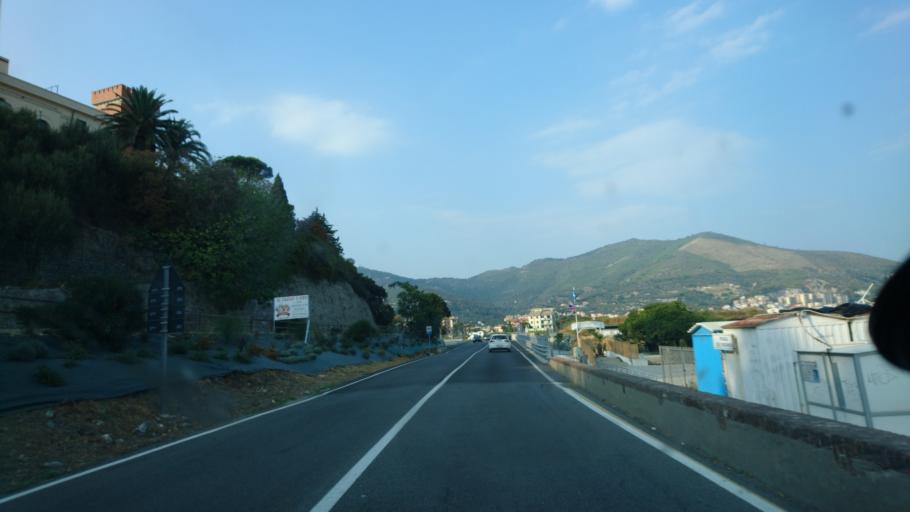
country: IT
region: Liguria
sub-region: Provincia di Savona
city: Spotorno
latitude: 44.2175
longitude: 8.4149
